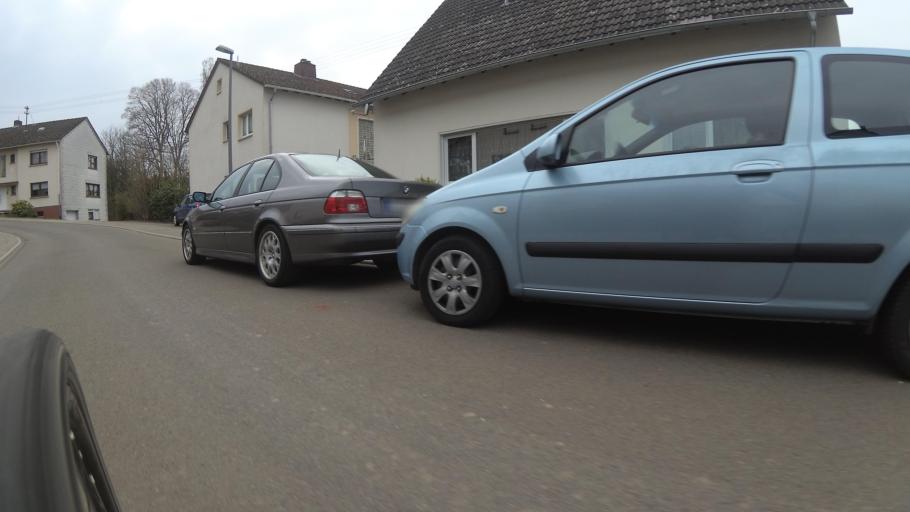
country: DE
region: Rheinland-Pfalz
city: Birkenfeld
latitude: 49.6426
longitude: 7.1677
